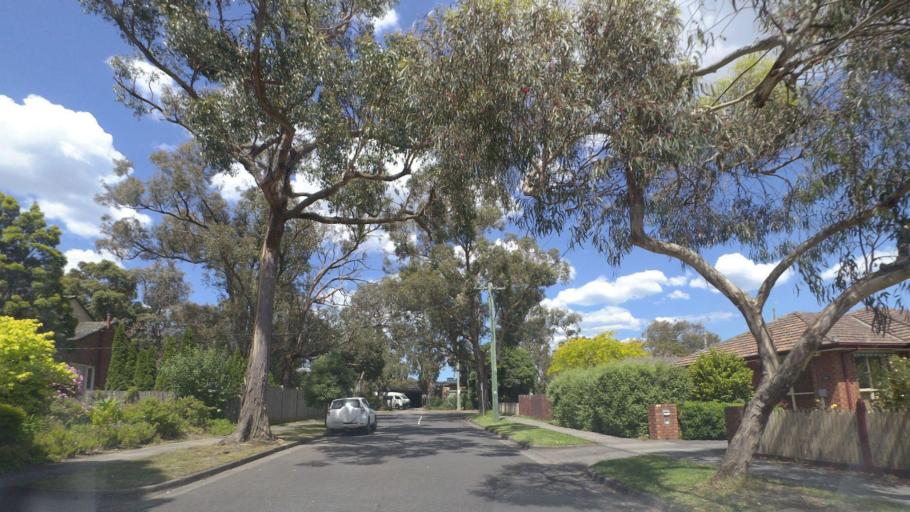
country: AU
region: Victoria
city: Mitcham
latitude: -37.8179
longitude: 145.2083
